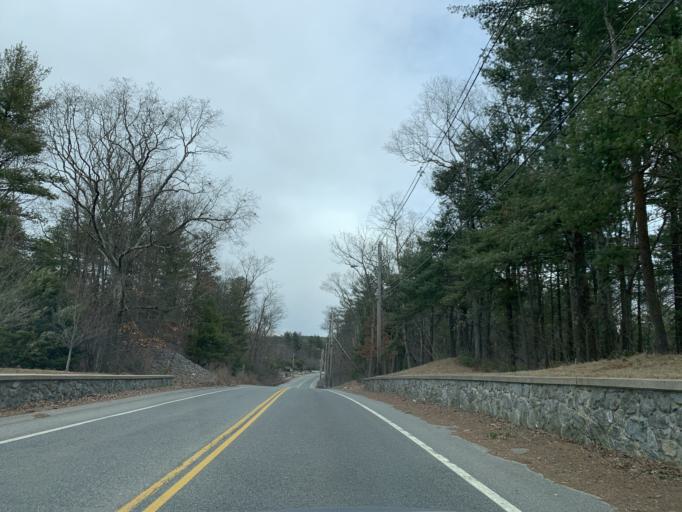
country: US
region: Massachusetts
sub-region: Norfolk County
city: Bellingham
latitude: 42.0357
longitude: -71.4751
